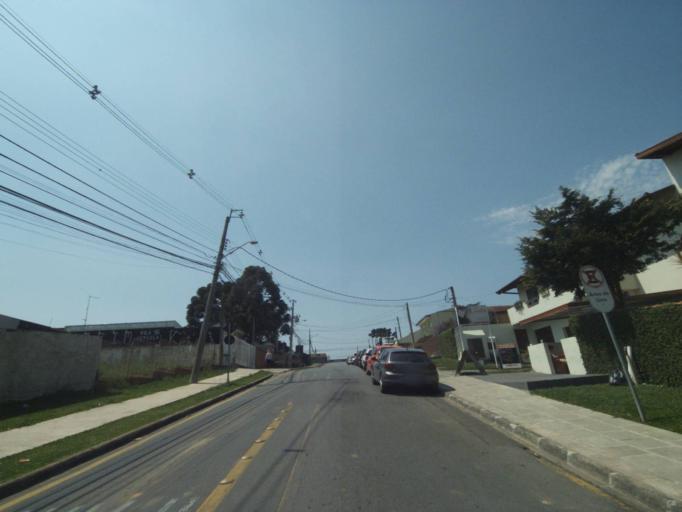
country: BR
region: Parana
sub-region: Curitiba
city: Curitiba
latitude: -25.4772
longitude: -49.3175
